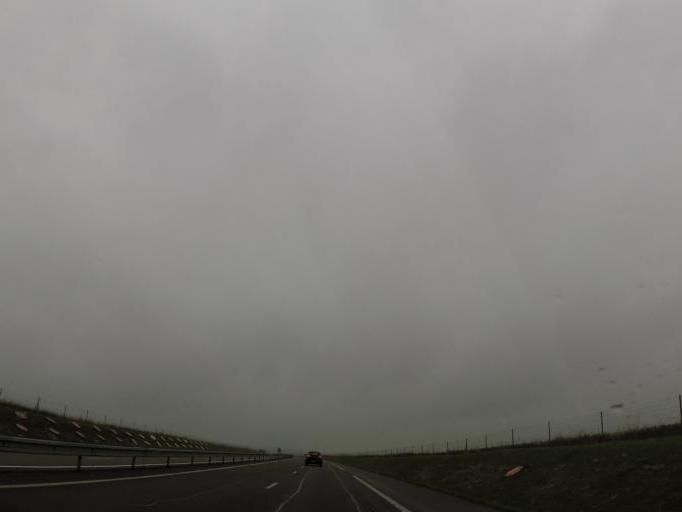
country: FR
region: Champagne-Ardenne
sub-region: Departement de la Marne
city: Courtisols
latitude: 49.0359
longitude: 4.5804
